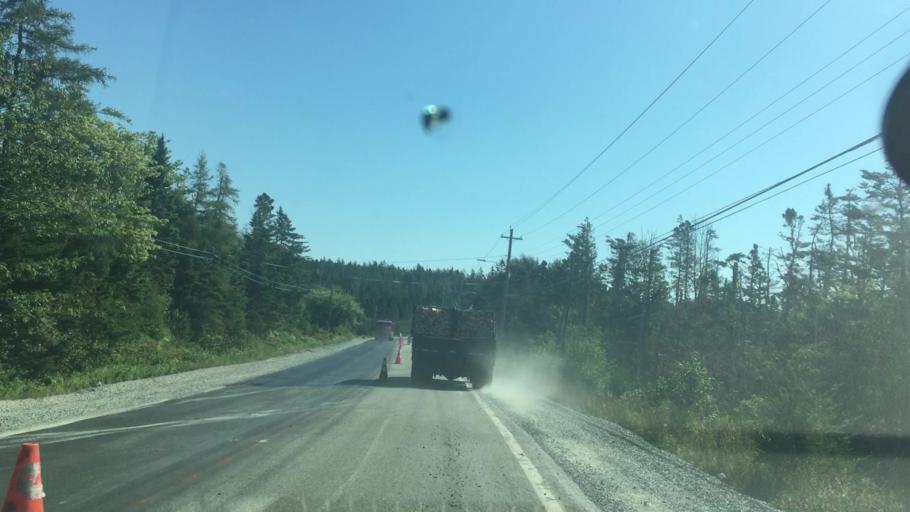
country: CA
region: Nova Scotia
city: New Glasgow
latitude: 44.9072
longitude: -62.4954
